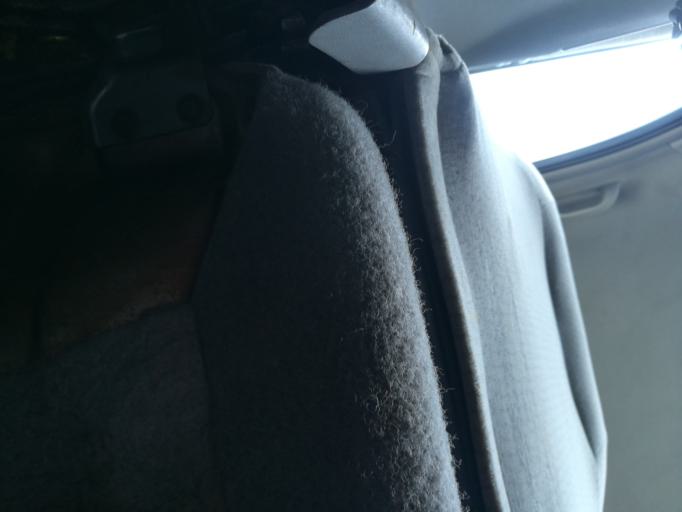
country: NG
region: Lagos
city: Ikoyi
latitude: 6.4411
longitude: 3.4202
